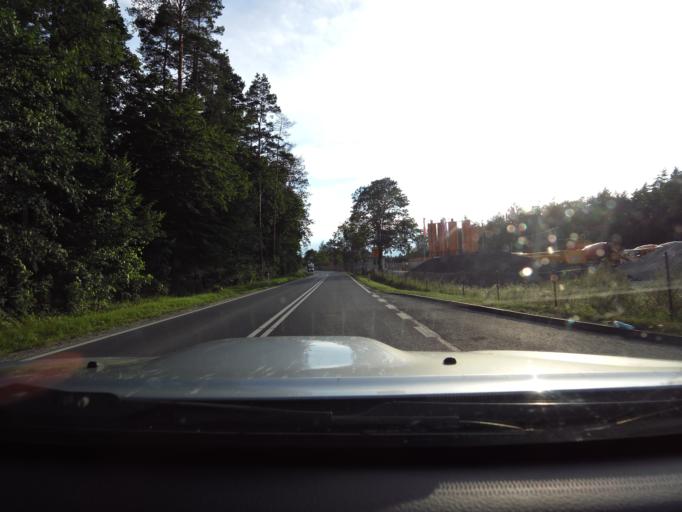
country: PL
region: Warmian-Masurian Voivodeship
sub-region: Powiat ostrodzki
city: Ostroda
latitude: 53.6926
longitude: 19.9072
